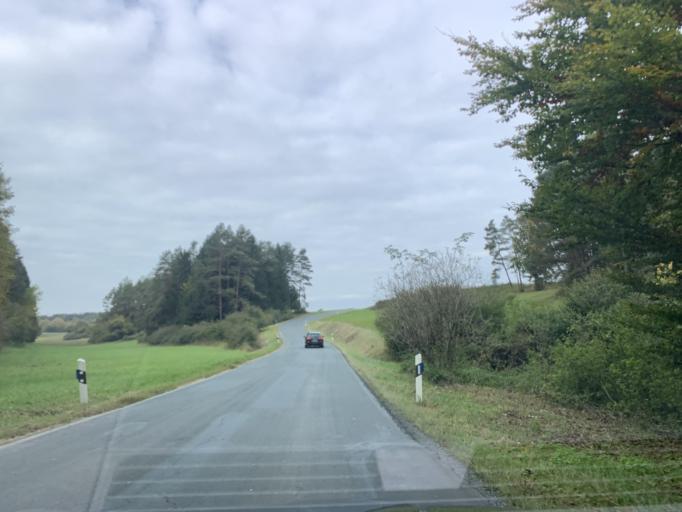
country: DE
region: Bavaria
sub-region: Upper Franconia
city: Pottenstein
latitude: 49.7387
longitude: 11.4084
